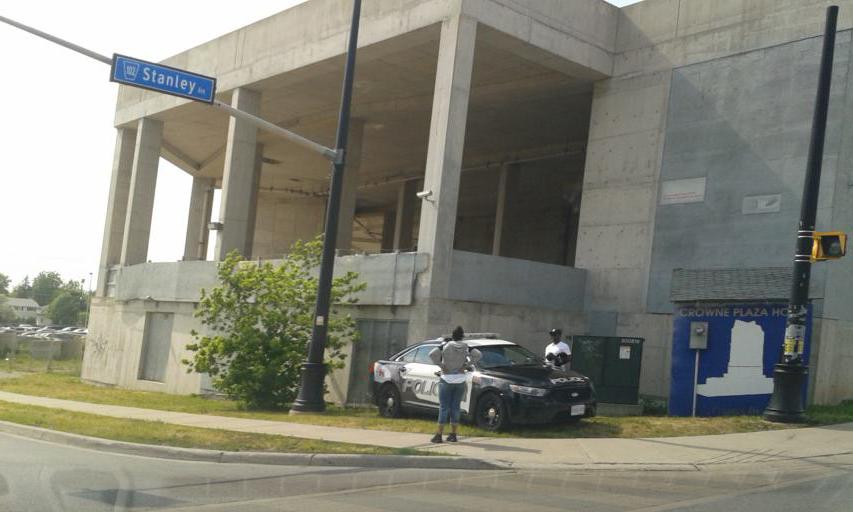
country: CA
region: Ontario
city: Niagara Falls
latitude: 43.0792
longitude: -79.0841
